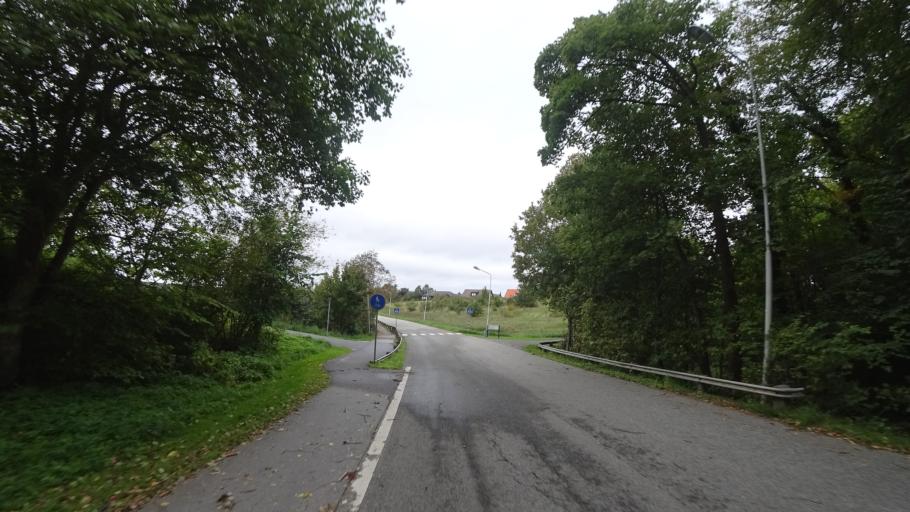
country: SE
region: Skane
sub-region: Kavlinge Kommun
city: Kaevlinge
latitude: 55.7758
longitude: 13.1100
